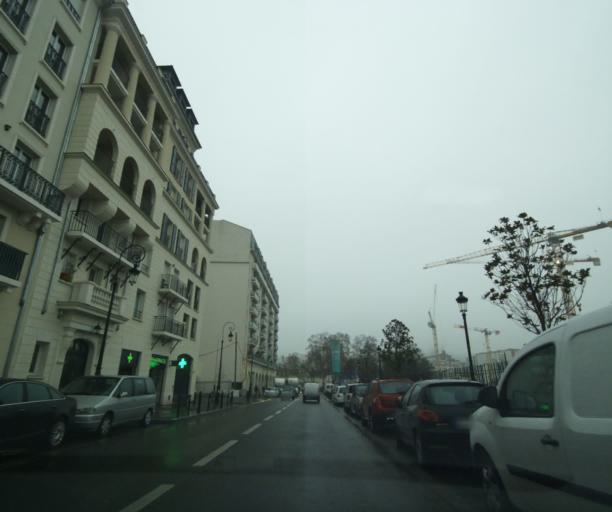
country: FR
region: Ile-de-France
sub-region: Departement des Hauts-de-Seine
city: Suresnes
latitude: 48.8838
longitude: 2.2252
